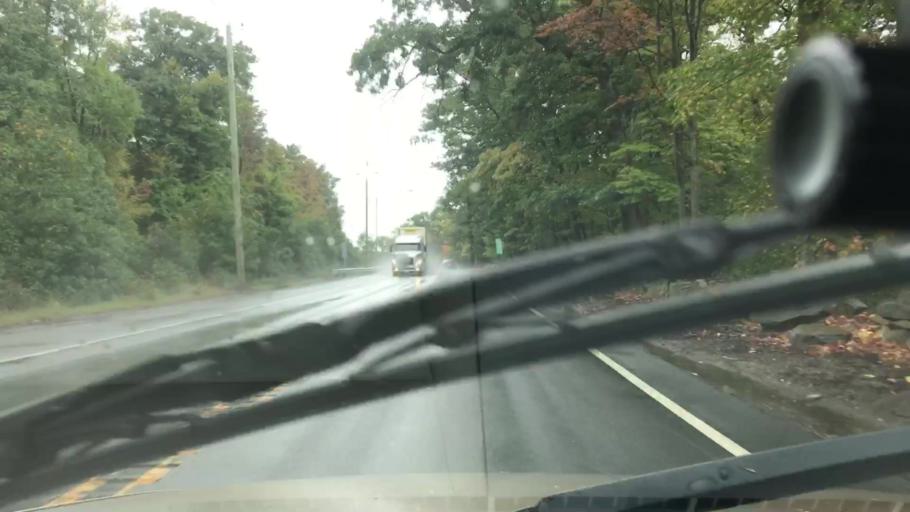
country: US
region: New Jersey
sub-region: Bergen County
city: Alpine
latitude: 40.9849
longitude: -73.9133
